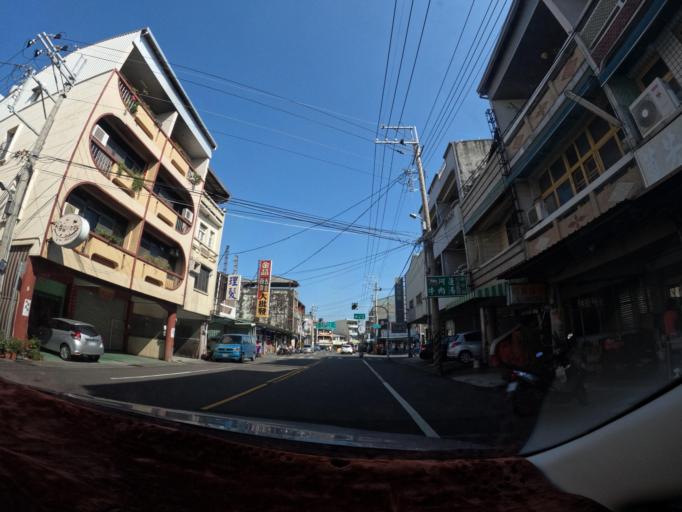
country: TW
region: Taiwan
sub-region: Tainan
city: Tainan
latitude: 23.0353
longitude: 120.3005
